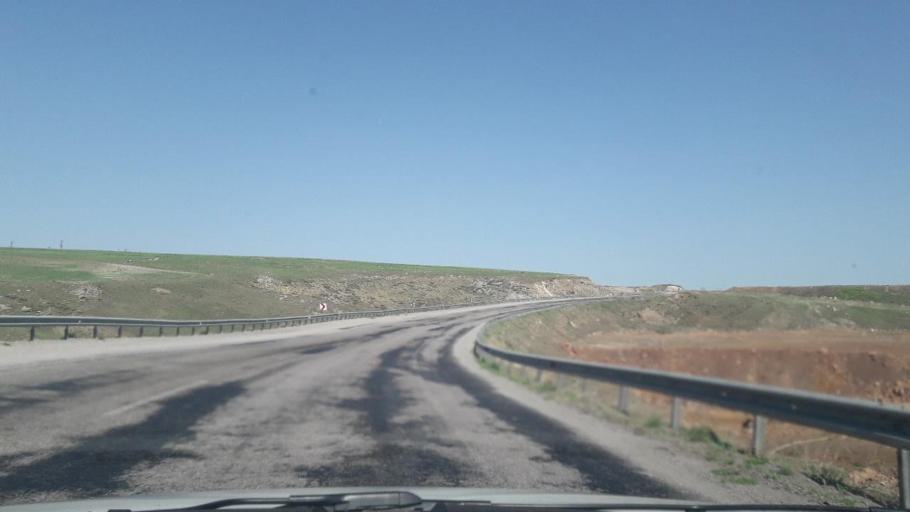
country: TR
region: Sivas
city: Kangal
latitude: 39.1660
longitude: 37.4727
